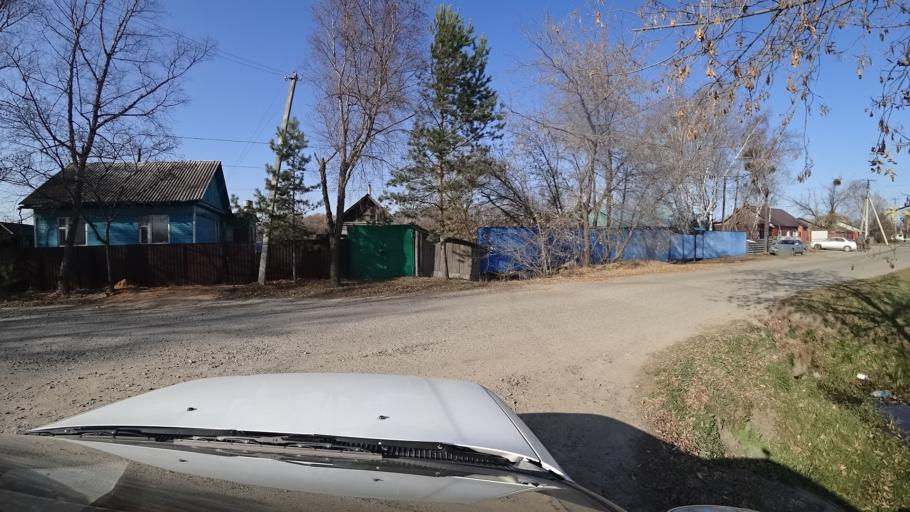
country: RU
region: Primorskiy
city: Dal'nerechensk
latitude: 45.9213
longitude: 133.7206
